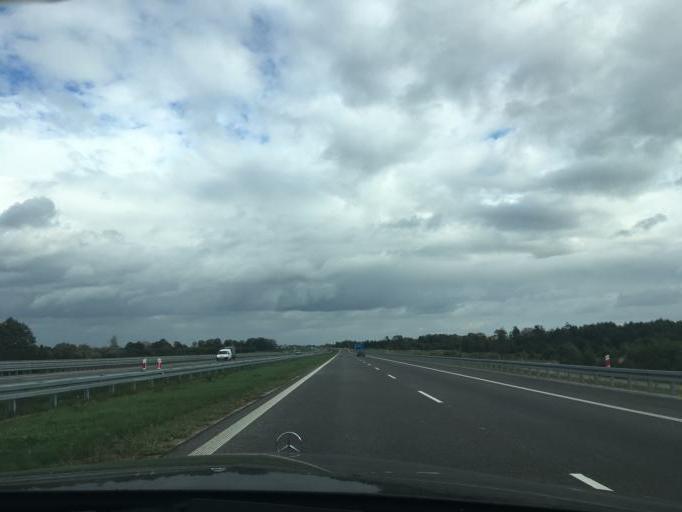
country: PL
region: Subcarpathian Voivodeship
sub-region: Powiat lancucki
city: Czarna
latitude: 50.0915
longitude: 22.1907
